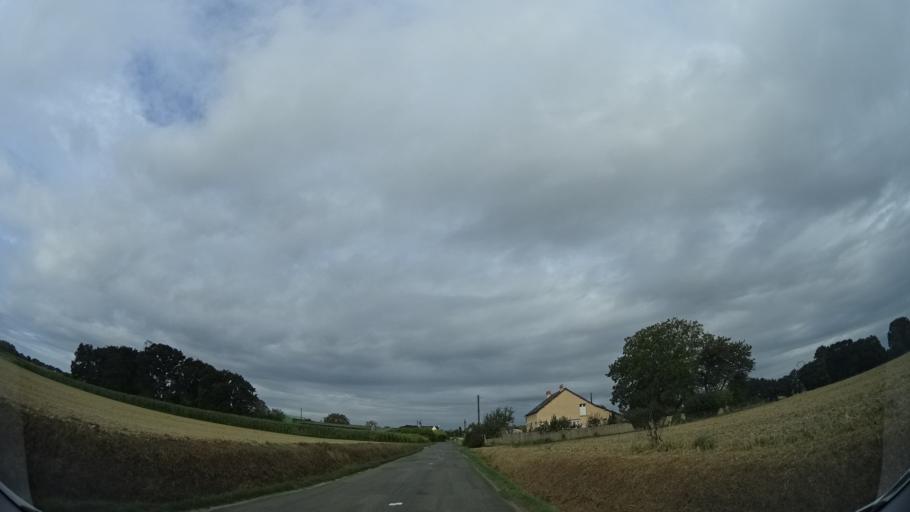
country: FR
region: Brittany
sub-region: Departement d'Ille-et-Vilaine
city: Hede-Bazouges
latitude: 48.2883
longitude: -1.8120
